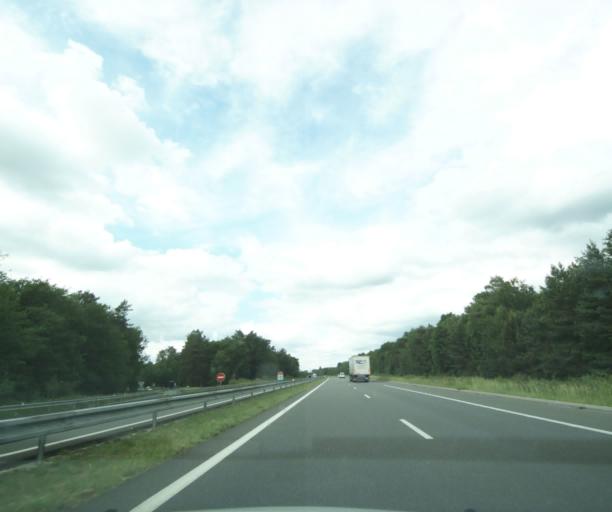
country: FR
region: Centre
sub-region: Departement du Loir-et-Cher
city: Salbris
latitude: 47.4676
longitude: 2.0072
